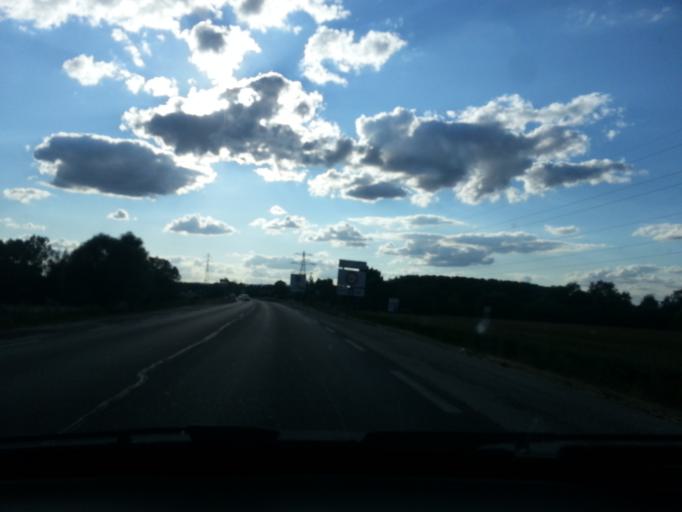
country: FR
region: Bourgogne
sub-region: Departement de Saone-et-Loire
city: Saint-Remy
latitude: 46.7585
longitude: 4.8495
